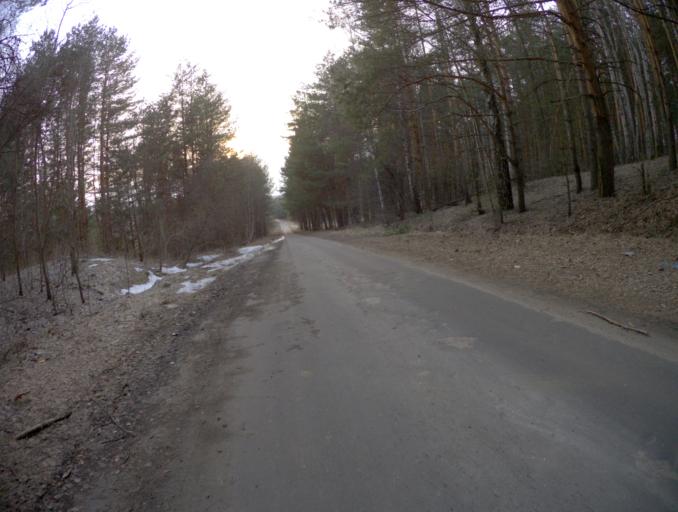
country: RU
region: Vladimir
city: Kommunar
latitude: 56.0675
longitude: 40.4389
